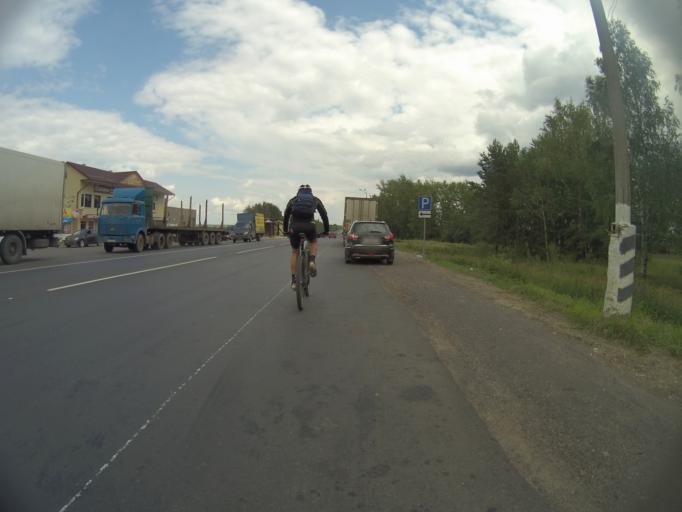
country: RU
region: Vladimir
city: Suzdal'
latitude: 56.4570
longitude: 40.4591
